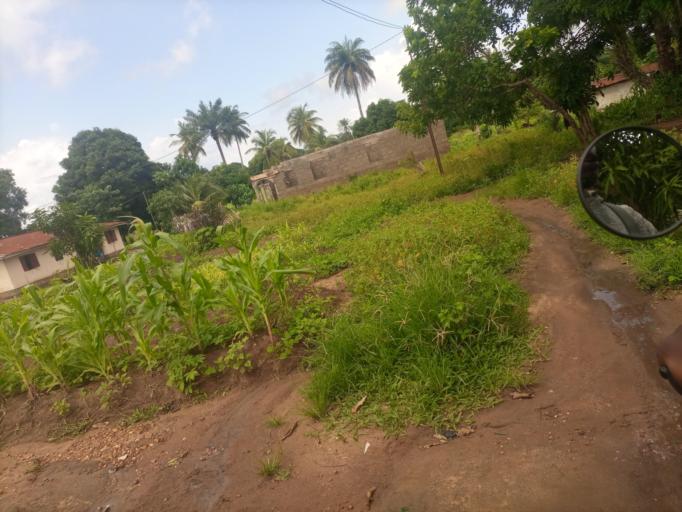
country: SL
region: Northern Province
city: Sawkta
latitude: 8.6327
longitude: -13.2095
